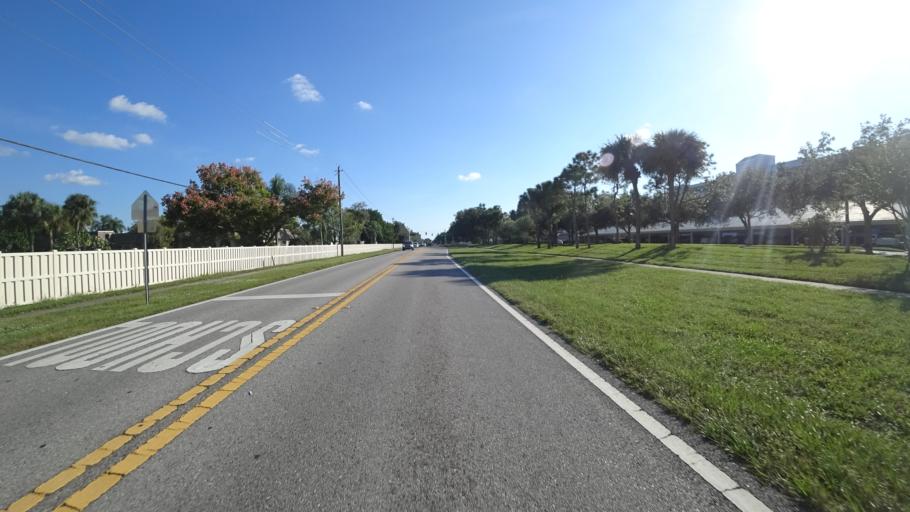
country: US
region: Florida
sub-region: Manatee County
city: South Bradenton
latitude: 27.4692
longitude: -82.6041
